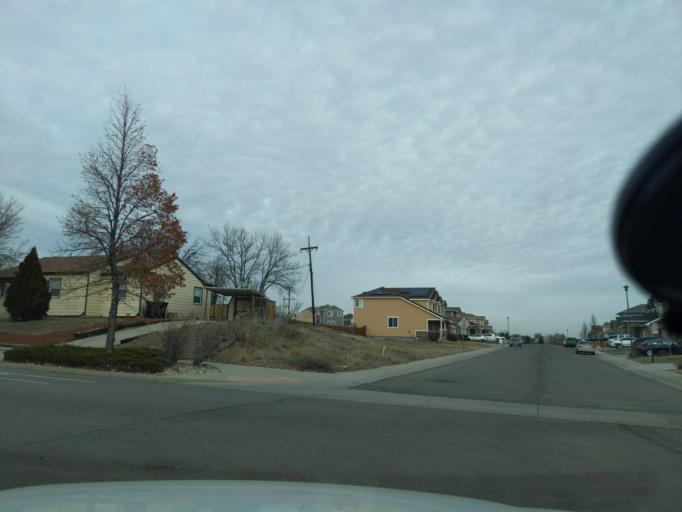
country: US
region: Colorado
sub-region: Adams County
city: Thornton
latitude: 39.8654
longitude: -104.9497
